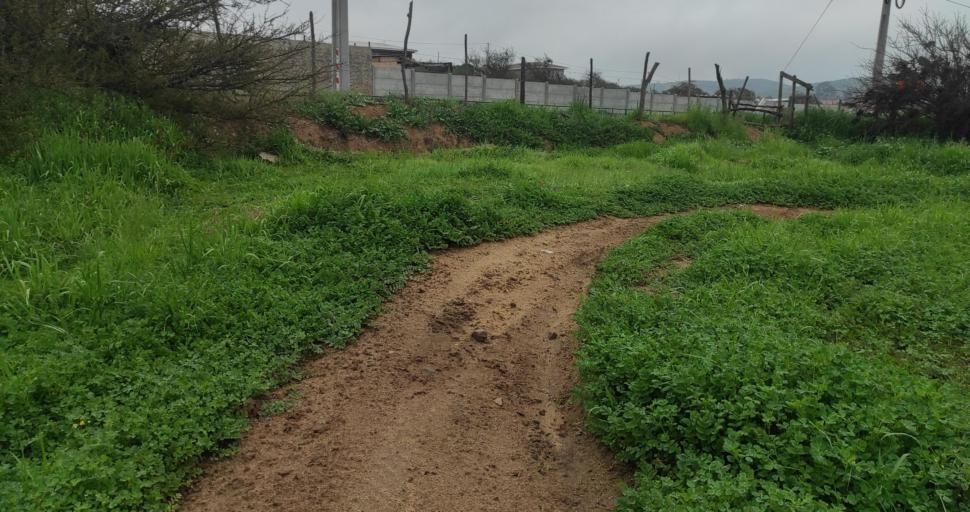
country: CL
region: Valparaiso
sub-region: Provincia de Marga Marga
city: Limache
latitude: -33.0221
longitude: -71.2606
